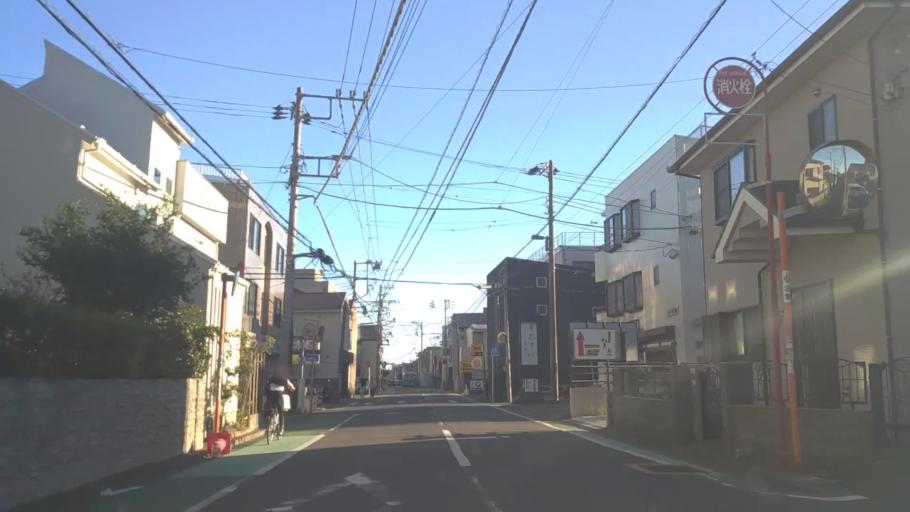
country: JP
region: Kanagawa
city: Chigasaki
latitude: 35.3292
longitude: 139.4145
